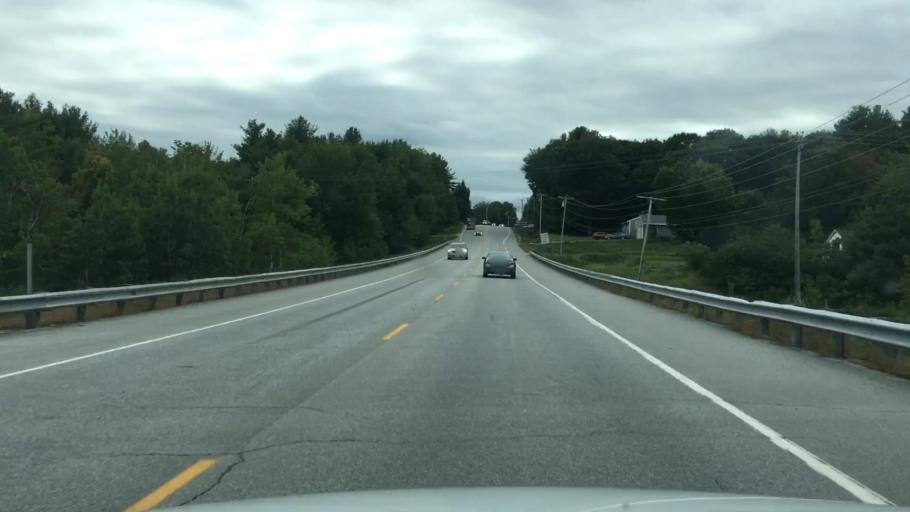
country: US
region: Maine
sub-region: Kennebec County
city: Gardiner
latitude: 44.2137
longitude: -69.8070
